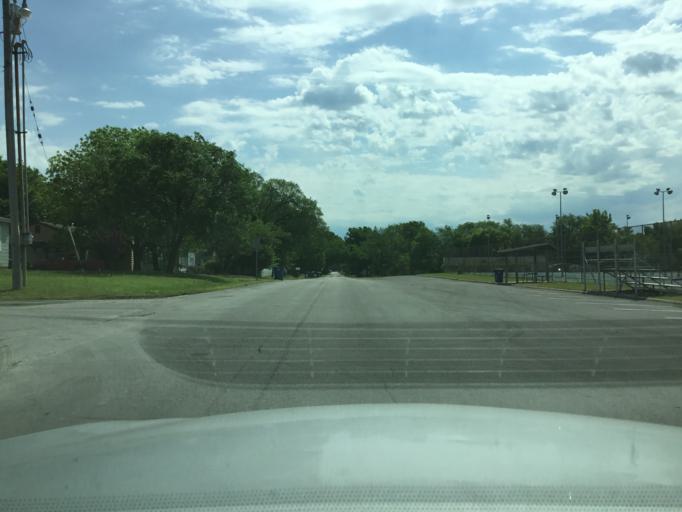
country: US
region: Kansas
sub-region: Montgomery County
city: Coffeyville
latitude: 37.0544
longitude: -95.6407
